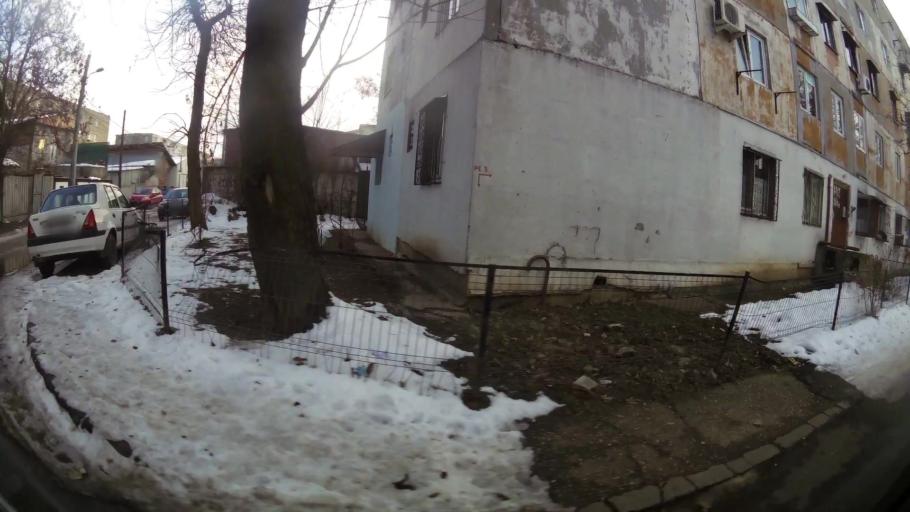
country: RO
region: Bucuresti
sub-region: Municipiul Bucuresti
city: Bucuresti
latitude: 44.3918
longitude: 26.0781
